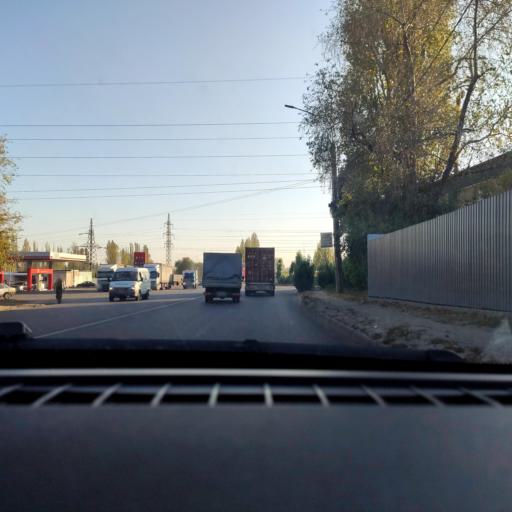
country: RU
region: Voronezj
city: Maslovka
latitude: 51.6293
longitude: 39.2619
